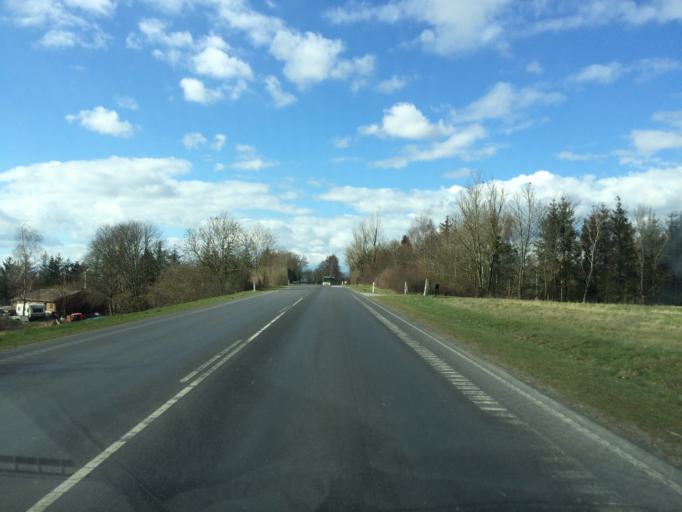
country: DK
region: South Denmark
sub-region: Assens Kommune
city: Arup
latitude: 55.4258
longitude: 10.0232
